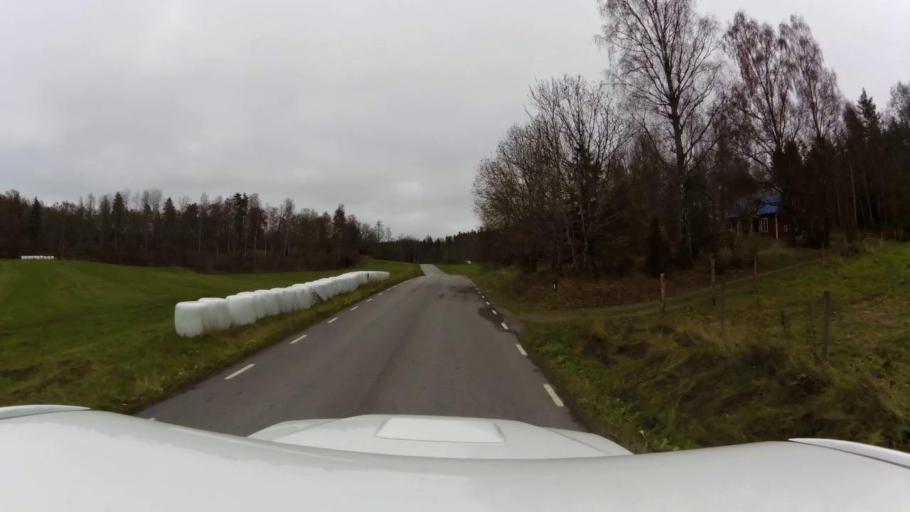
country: SE
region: OEstergoetland
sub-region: Kinda Kommun
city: Rimforsa
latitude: 58.1429
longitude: 15.6417
